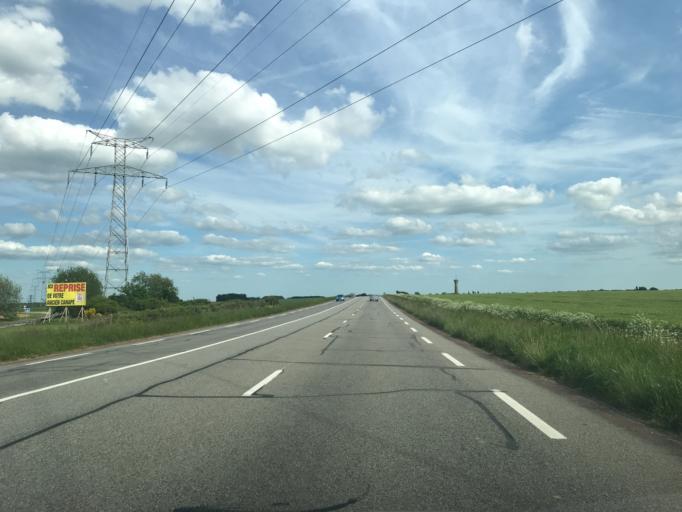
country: FR
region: Haute-Normandie
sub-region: Departement de l'Eure
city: Saint-Sebastien-de-Morsent
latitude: 49.0418
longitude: 1.0802
